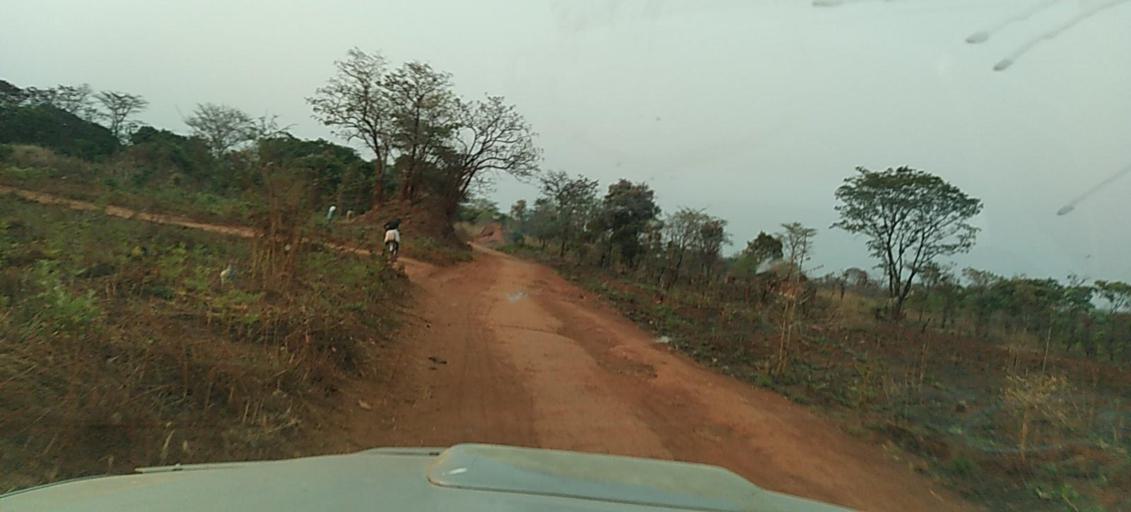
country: ZM
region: North-Western
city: Kasempa
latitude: -13.0628
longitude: 26.3819
